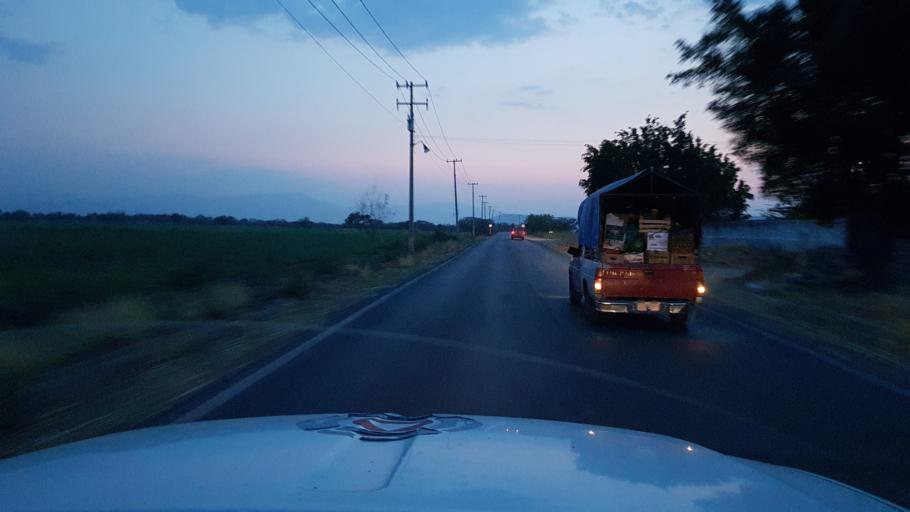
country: MX
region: Morelos
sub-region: Tlaquiltenango
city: Alfredo V. Bonfil (Chacampalco)
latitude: 18.6865
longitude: -99.1553
